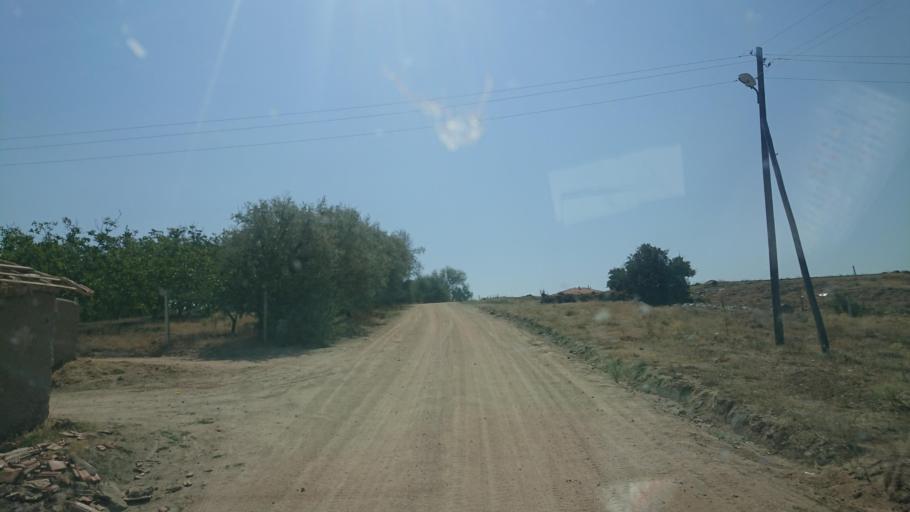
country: TR
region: Aksaray
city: Agacoren
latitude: 38.8164
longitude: 33.9543
